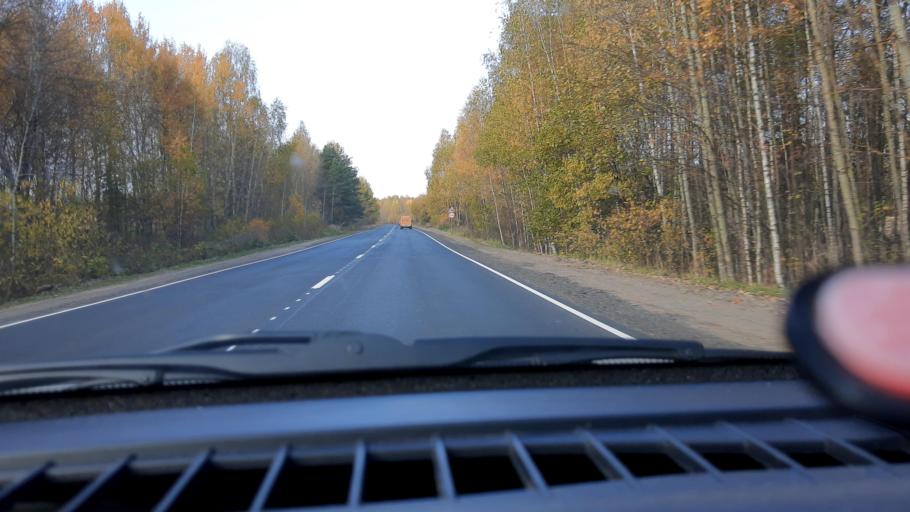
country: RU
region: Nizjnij Novgorod
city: Lukino
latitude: 56.5462
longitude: 43.7579
